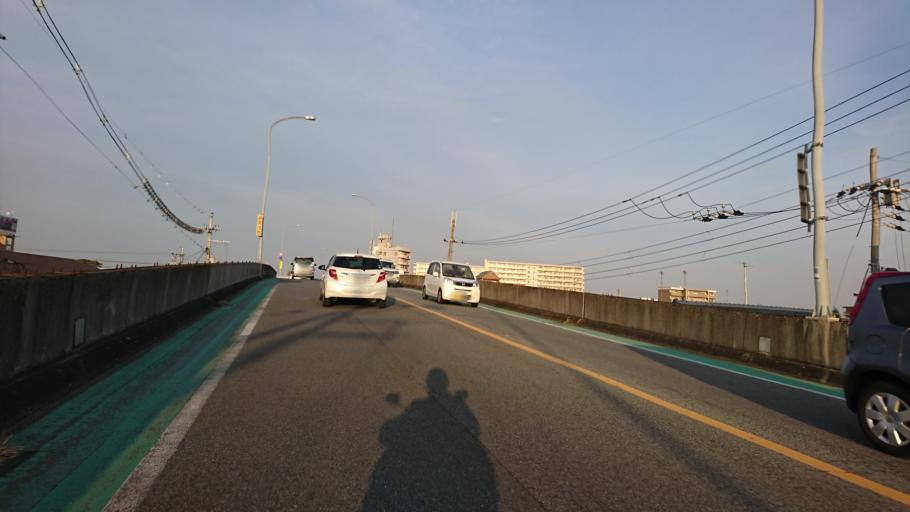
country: JP
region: Hyogo
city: Kakogawacho-honmachi
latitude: 34.7477
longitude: 134.8662
